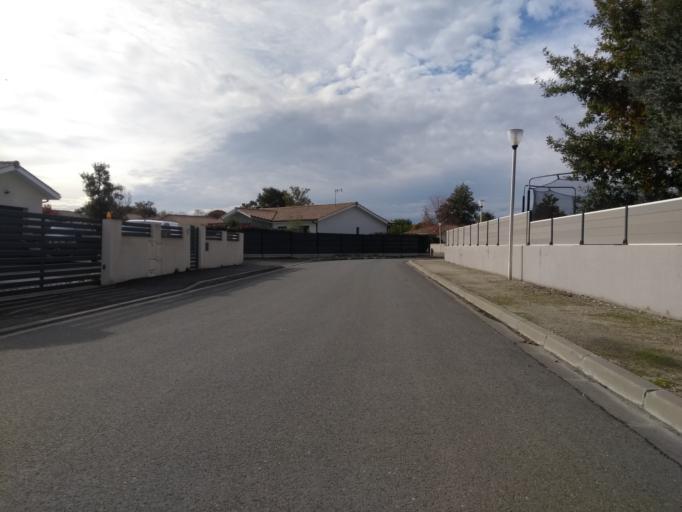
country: FR
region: Aquitaine
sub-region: Departement de la Gironde
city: Cestas
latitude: 44.7383
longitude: -0.6715
